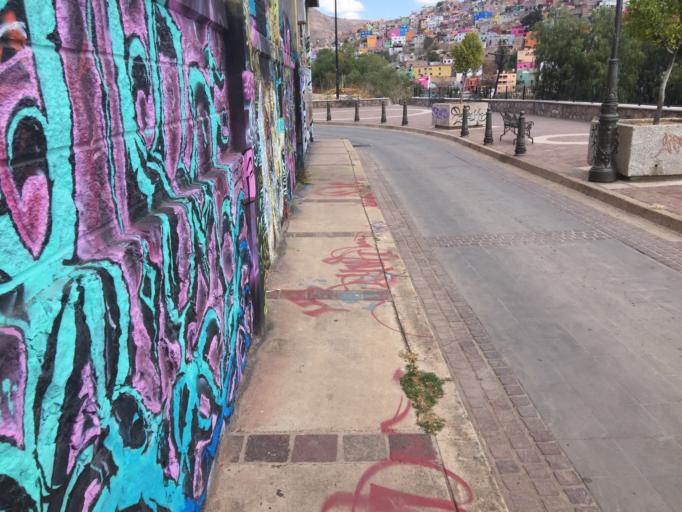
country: MX
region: Guanajuato
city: Guanajuato
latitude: 21.0167
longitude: -101.2663
